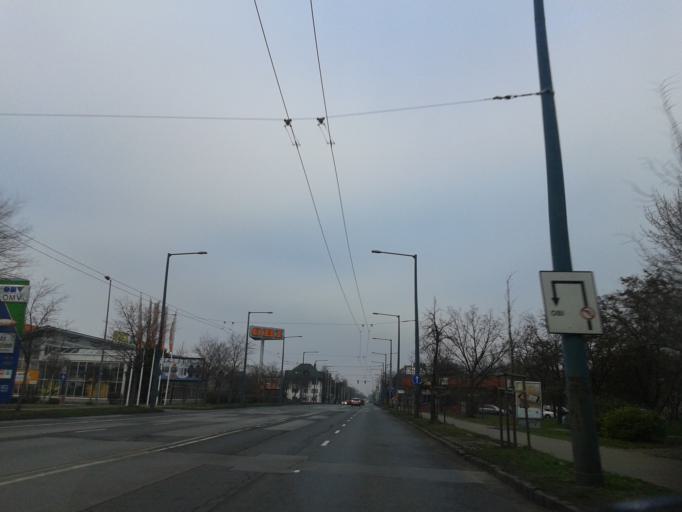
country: HU
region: Budapest
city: Budapest XIV. keruelet
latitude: 47.5046
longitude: 19.1207
